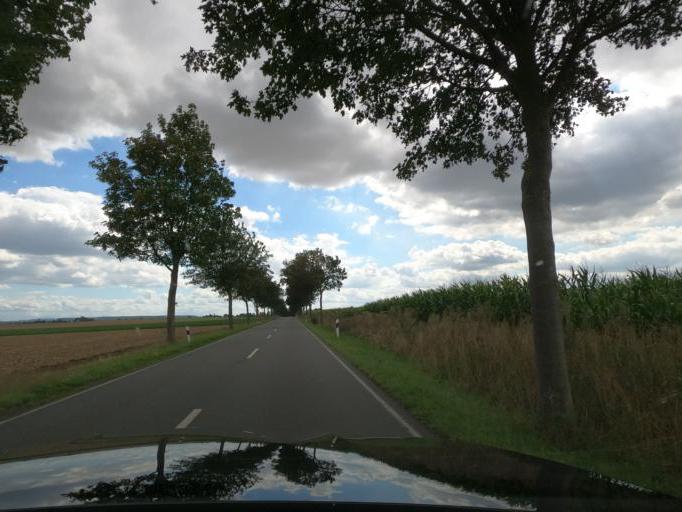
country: DE
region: Lower Saxony
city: Ilsede
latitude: 52.2259
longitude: 10.1752
